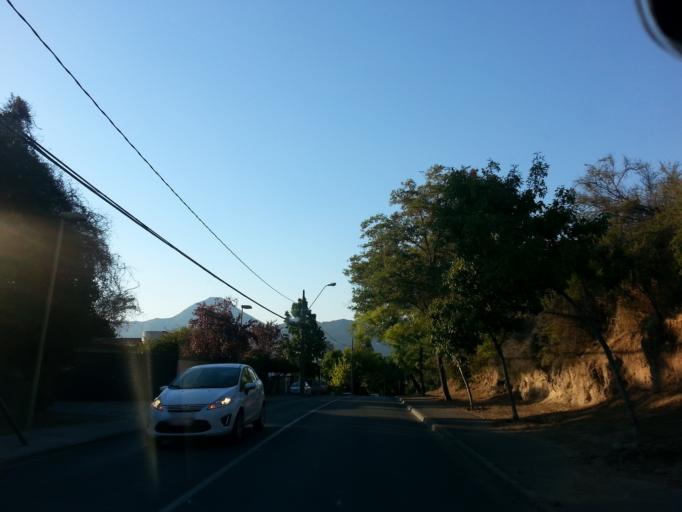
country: CL
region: Santiago Metropolitan
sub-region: Provincia de Santiago
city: Villa Presidente Frei, Nunoa, Santiago, Chile
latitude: -33.4024
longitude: -70.5396
